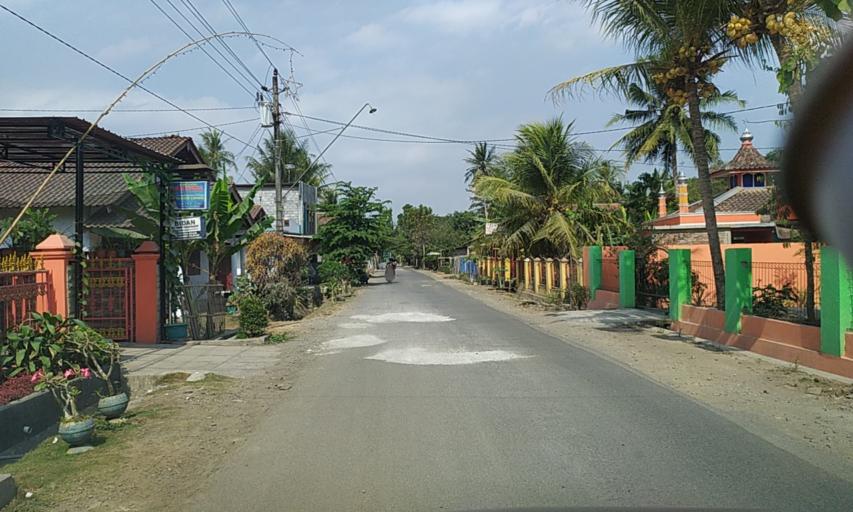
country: ID
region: Central Java
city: Kemantren Satu
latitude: -7.5241
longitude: 108.8610
